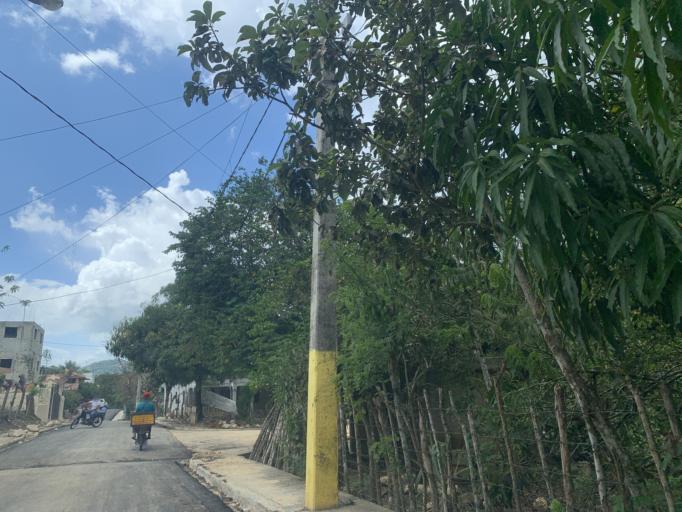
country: DO
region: Monte Plata
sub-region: Yamasa
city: Yamasa
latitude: 18.7798
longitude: -70.0260
